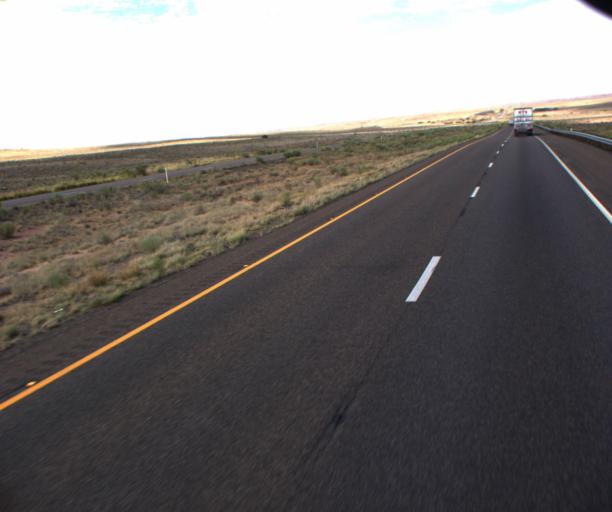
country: US
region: Arizona
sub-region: Navajo County
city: Holbrook
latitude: 35.0885
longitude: -109.6943
